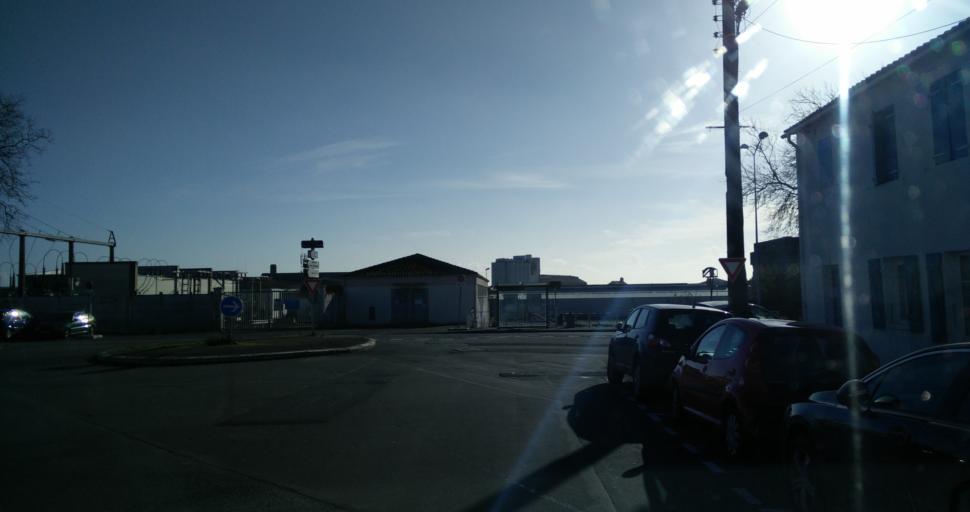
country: FR
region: Poitou-Charentes
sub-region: Departement de la Charente-Maritime
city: La Rochelle
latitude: 46.1617
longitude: -1.2073
